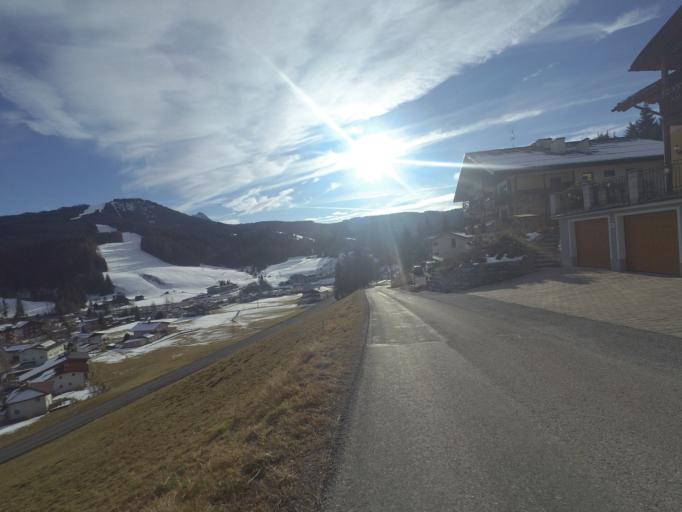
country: AT
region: Salzburg
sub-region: Politischer Bezirk Hallein
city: Abtenau
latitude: 47.5936
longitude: 13.4632
